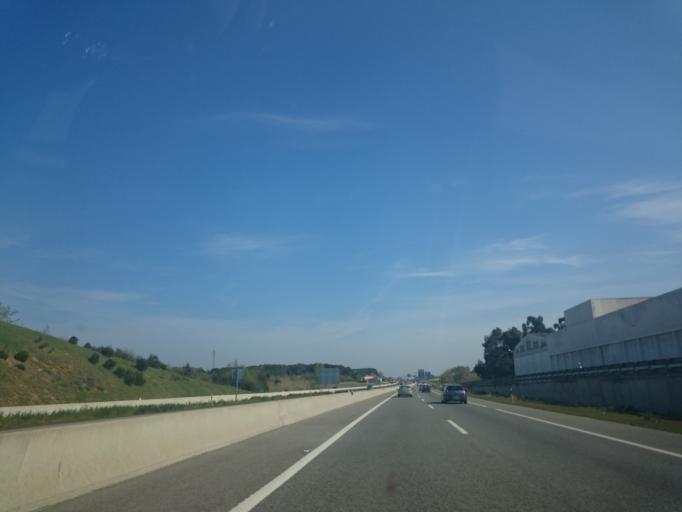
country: ES
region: Catalonia
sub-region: Provincia de Girona
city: Riudellots de la Selva
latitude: 41.9120
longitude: 2.7905
